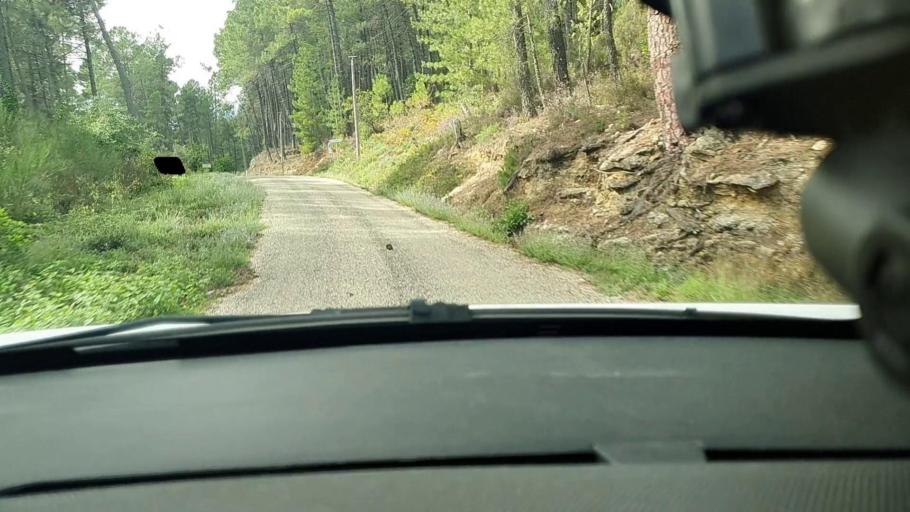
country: FR
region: Languedoc-Roussillon
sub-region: Departement du Gard
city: Branoux-les-Taillades
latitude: 44.2359
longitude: 3.9692
